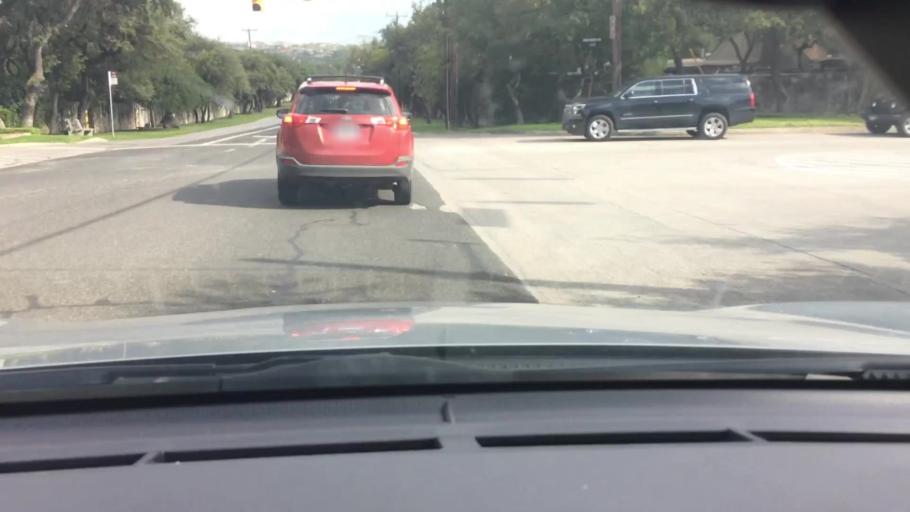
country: US
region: Texas
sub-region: Bexar County
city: Shavano Park
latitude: 29.5594
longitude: -98.5518
